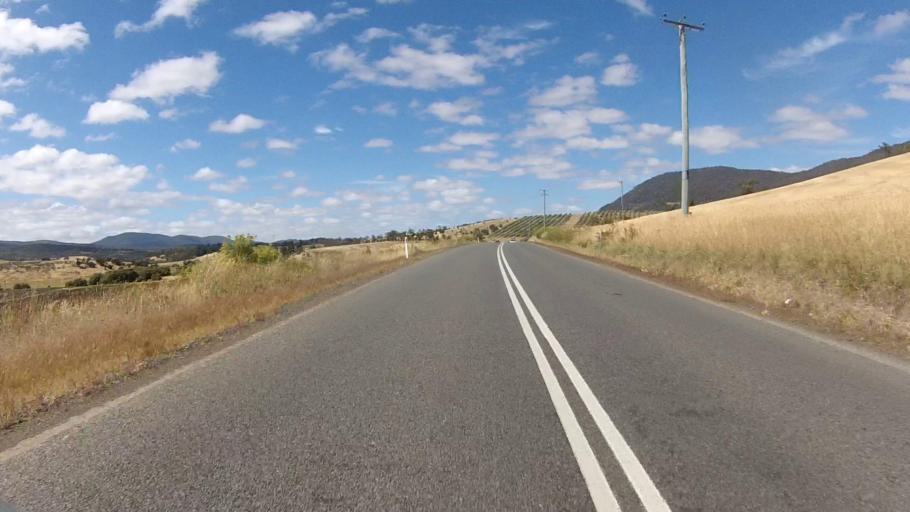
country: AU
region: Tasmania
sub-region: Brighton
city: Old Beach
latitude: -42.5992
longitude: 147.4159
